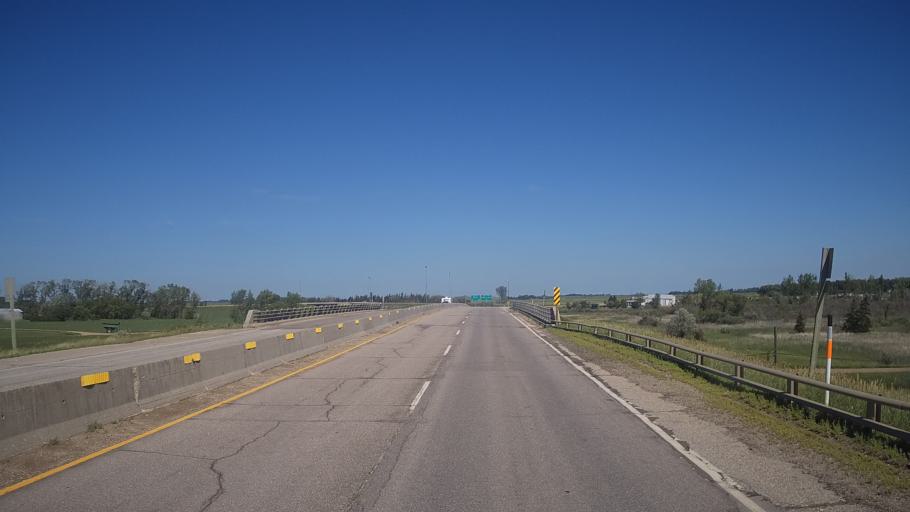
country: CA
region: Manitoba
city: Portage la Prairie
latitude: 49.9670
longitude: -98.3567
